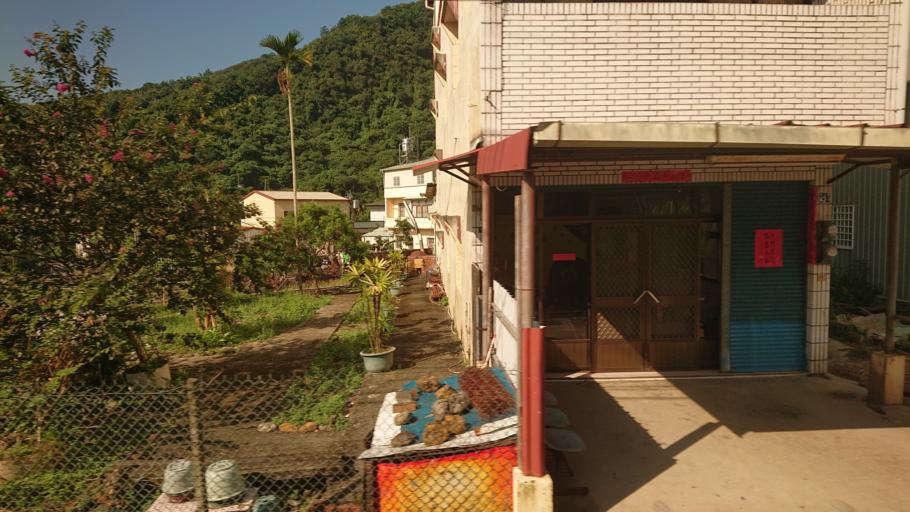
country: TW
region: Taiwan
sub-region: Nantou
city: Puli
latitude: 24.0588
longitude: 120.9024
